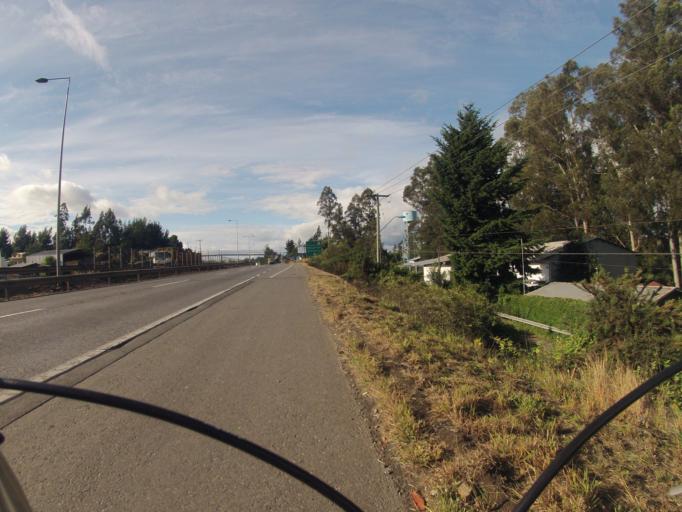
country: CL
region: Araucania
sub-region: Provincia de Cautin
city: Temuco
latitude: -38.8213
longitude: -72.6233
